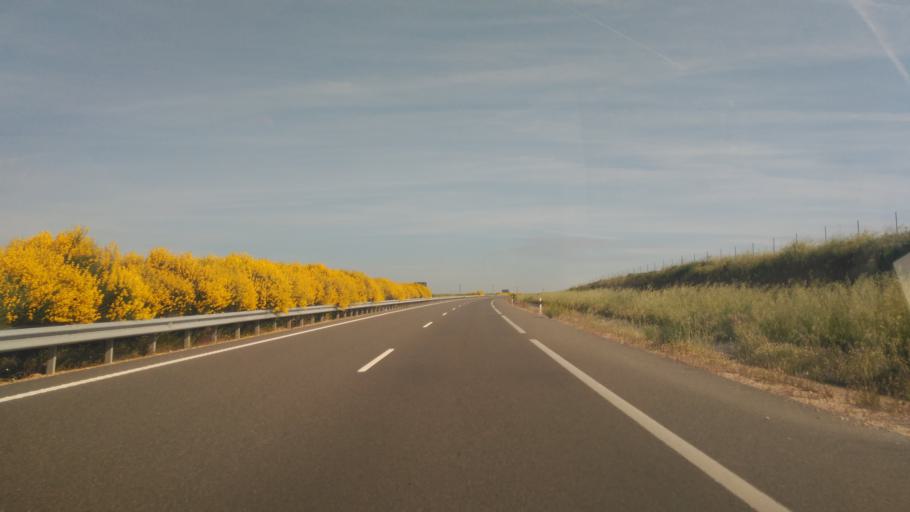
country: ES
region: Castille and Leon
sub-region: Provincia de Salamanca
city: Calzada de Valdunciel
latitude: 41.0973
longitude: -5.6964
